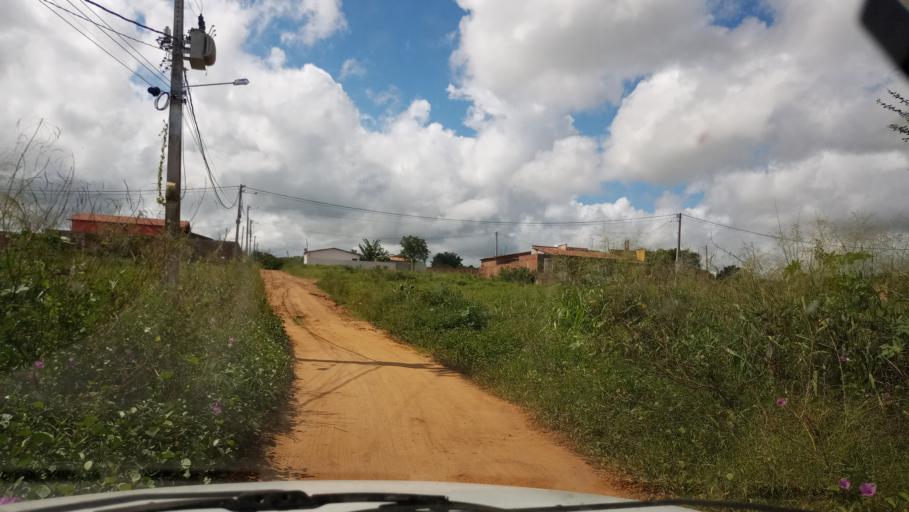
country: BR
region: Rio Grande do Norte
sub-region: Brejinho
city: Brejinho
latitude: -6.1469
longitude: -35.4323
